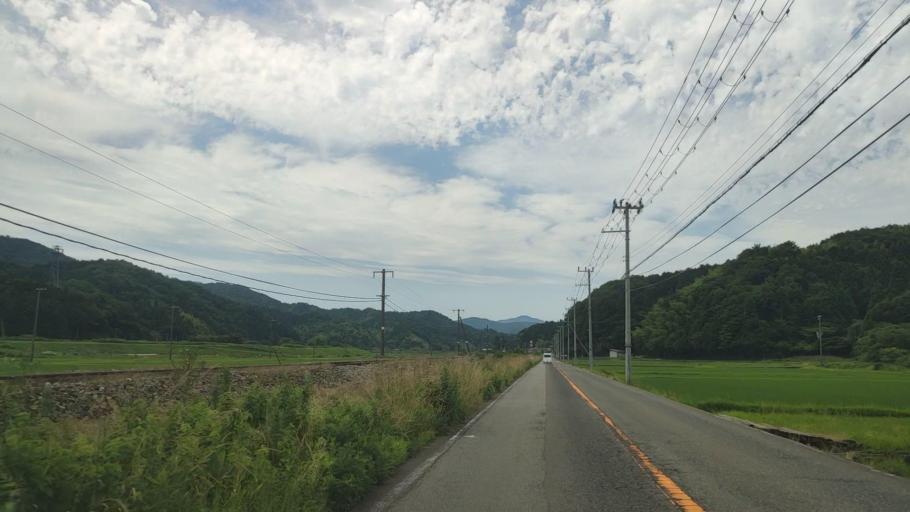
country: JP
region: Hyogo
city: Toyooka
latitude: 35.6394
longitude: 134.7577
